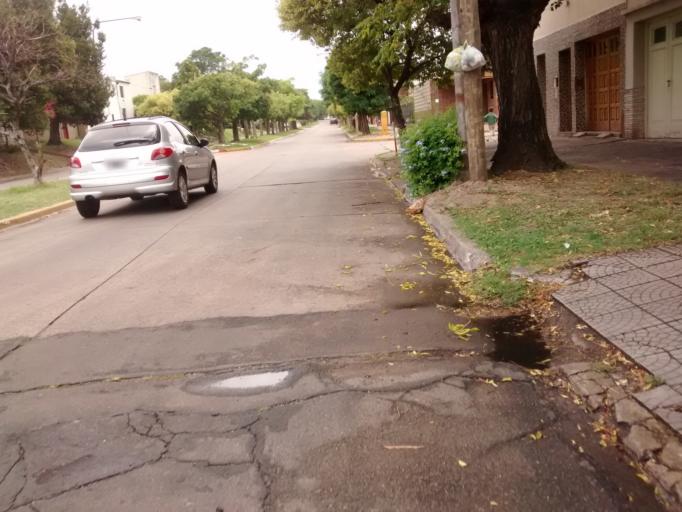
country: AR
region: Buenos Aires
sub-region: Partido de La Plata
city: La Plata
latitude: -34.8955
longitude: -57.9710
